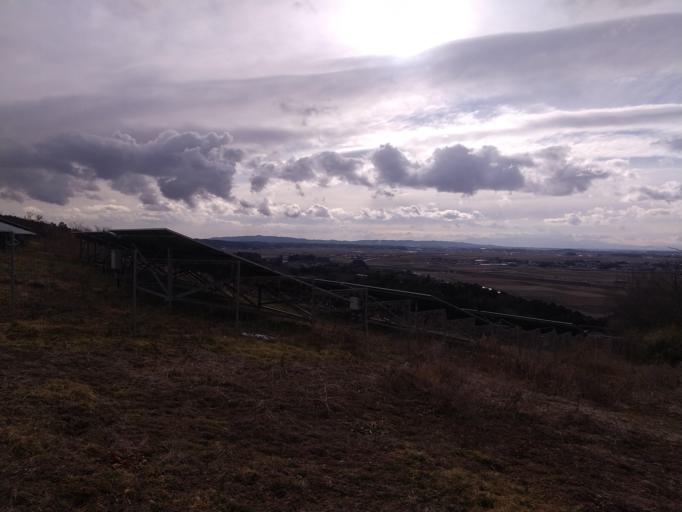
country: JP
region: Miyagi
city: Wakuya
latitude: 38.6838
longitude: 141.2801
